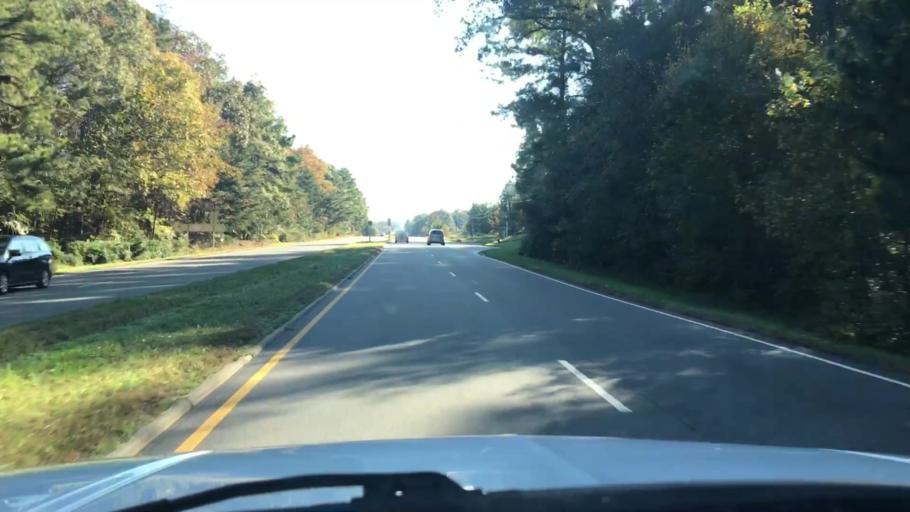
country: US
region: Virginia
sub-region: Henrico County
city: Short Pump
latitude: 37.5984
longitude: -77.6355
